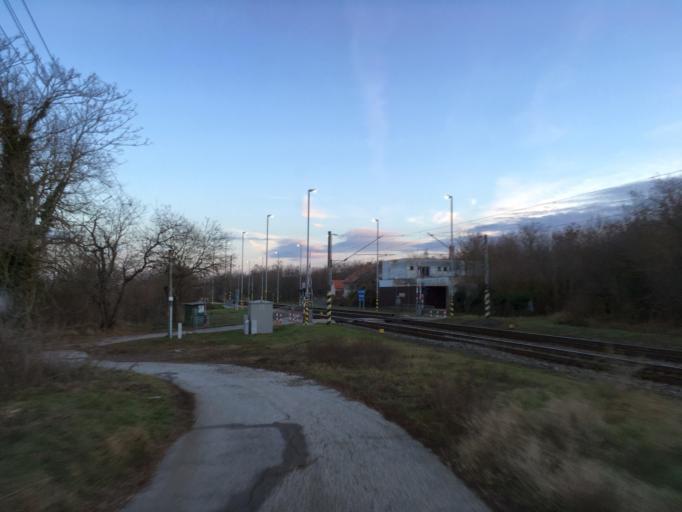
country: SK
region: Nitriansky
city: Svodin
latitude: 47.8693
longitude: 18.4602
